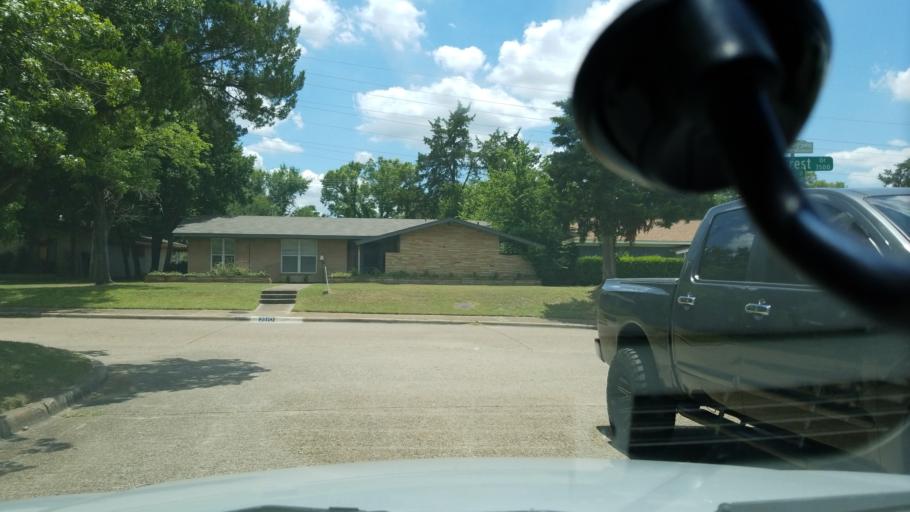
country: US
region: Texas
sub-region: Dallas County
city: Cockrell Hill
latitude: 32.7018
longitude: -96.8788
